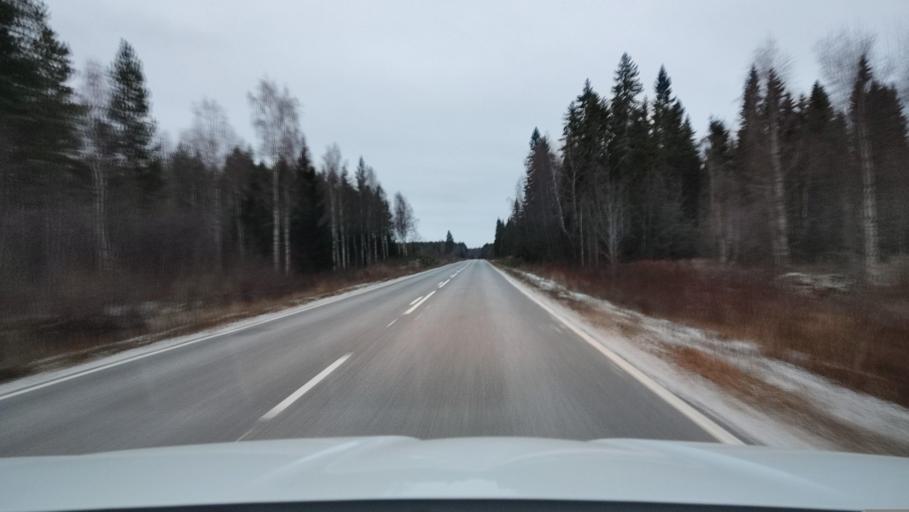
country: FI
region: Ostrobothnia
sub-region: Vaasa
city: Replot
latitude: 63.2465
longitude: 21.3787
